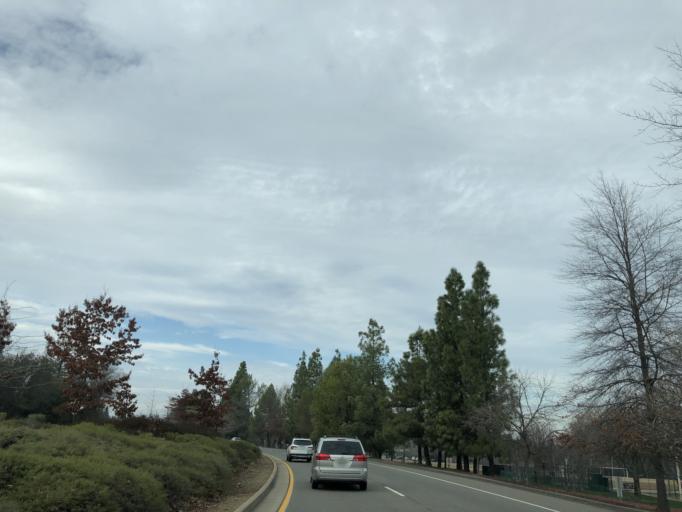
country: US
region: California
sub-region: El Dorado County
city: El Dorado Hills
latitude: 38.6832
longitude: -121.0761
